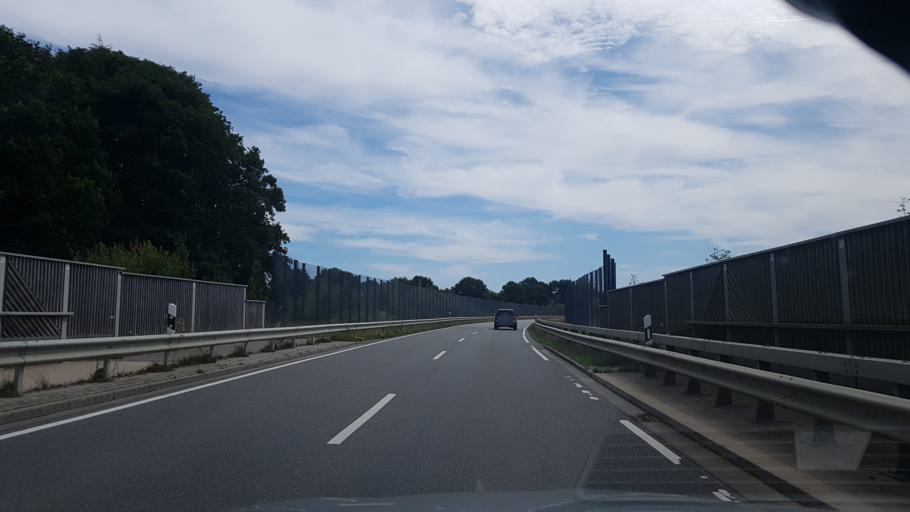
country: DE
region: Schleswig-Holstein
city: Nettelsee
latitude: 54.1710
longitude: 10.1910
